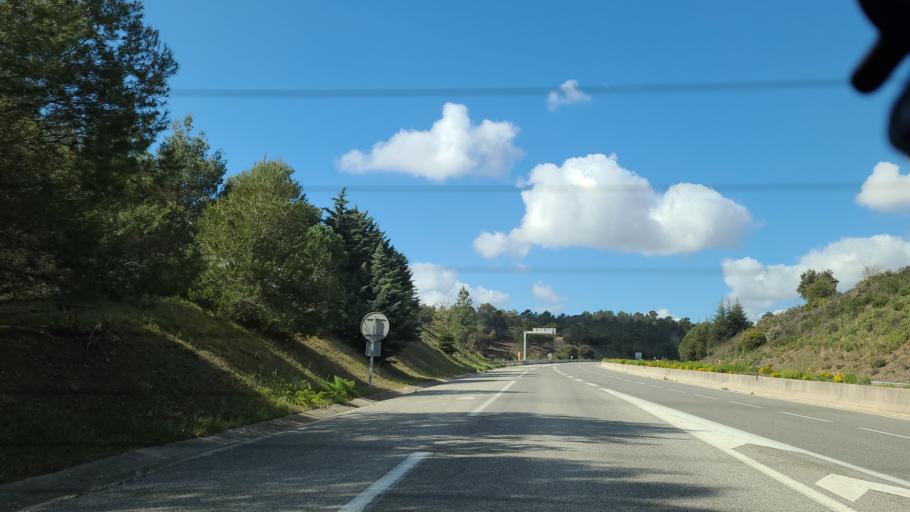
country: FR
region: Provence-Alpes-Cote d'Azur
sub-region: Departement du Var
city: Carnoules
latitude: 43.2714
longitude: 6.1822
